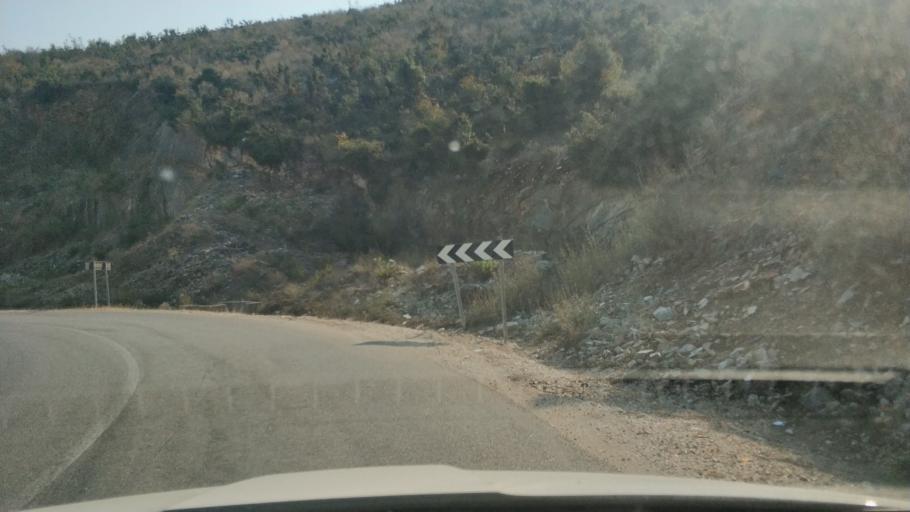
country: AL
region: Vlore
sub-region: Rrethi i Sarandes
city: Sarande
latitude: 39.8552
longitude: 20.0348
